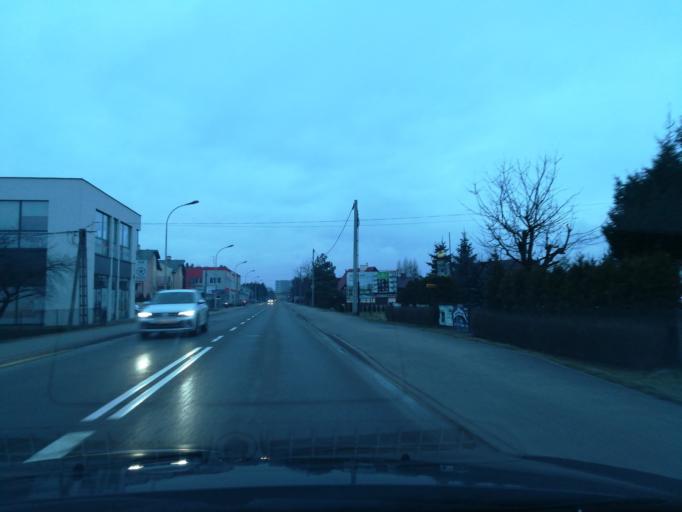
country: PL
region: Subcarpathian Voivodeship
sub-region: Rzeszow
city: Rzeszow
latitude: 50.0062
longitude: 22.0062
